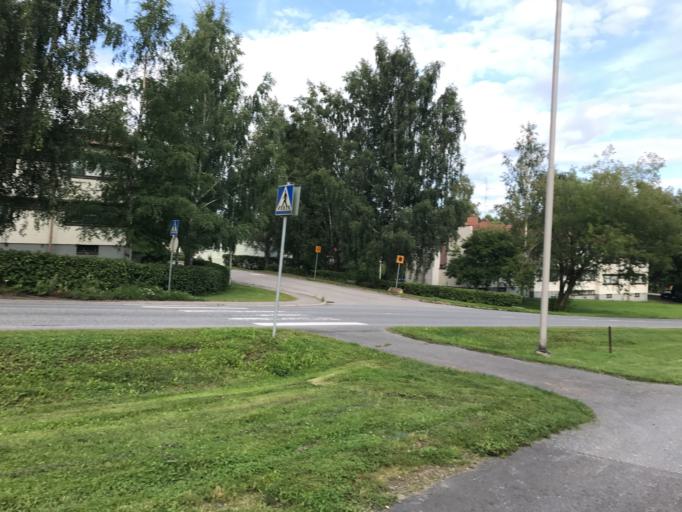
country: FI
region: Pirkanmaa
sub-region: Etelae-Pirkanmaa
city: Valkeakoski
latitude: 61.2555
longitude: 24.0396
